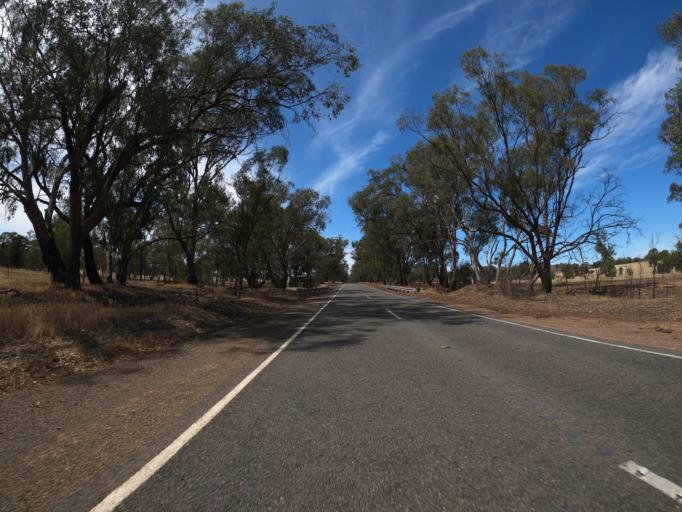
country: AU
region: Victoria
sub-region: Benalla
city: Benalla
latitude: -36.3593
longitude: 145.9669
